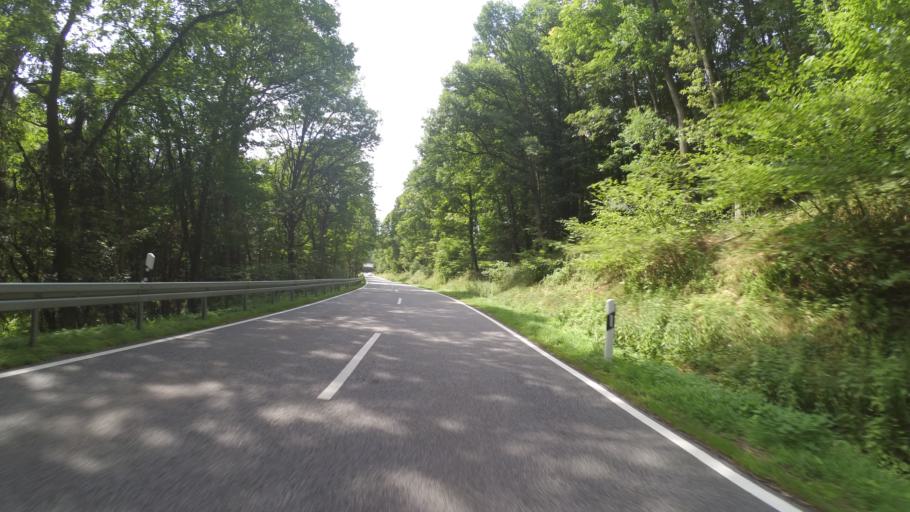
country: DE
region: Saarland
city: Tholey
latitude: 49.5298
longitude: 6.9998
